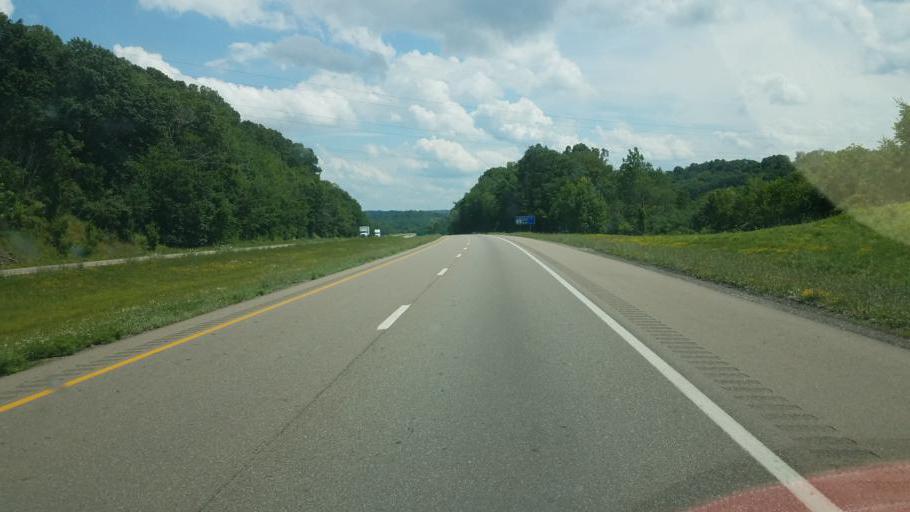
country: US
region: Ohio
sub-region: Tuscarawas County
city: Newcomerstown
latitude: 40.3063
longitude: -81.5667
